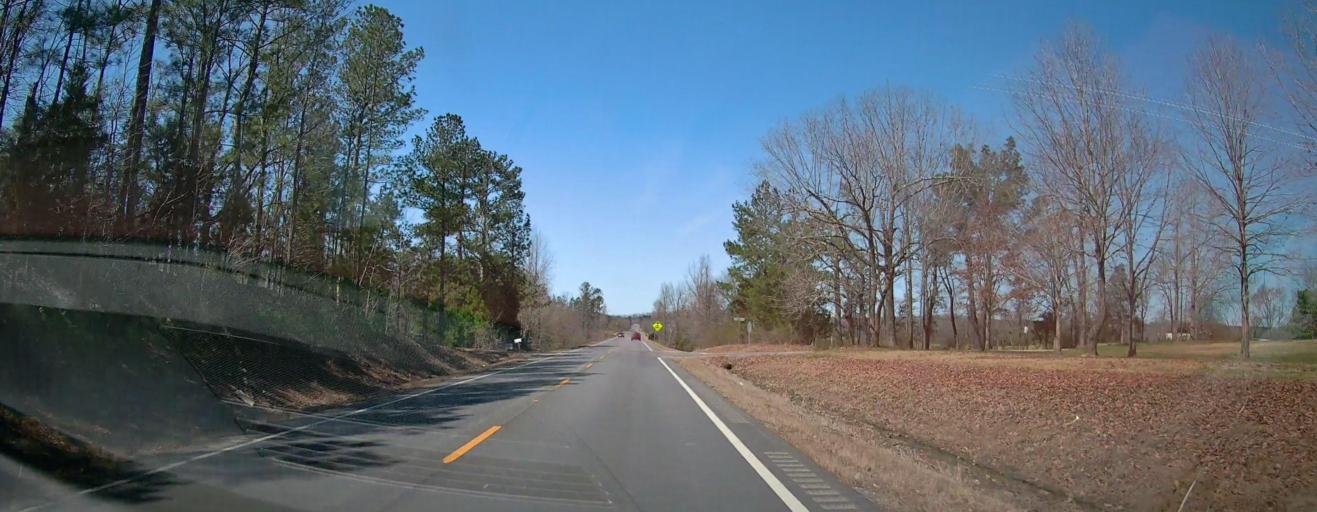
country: US
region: Alabama
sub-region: Calhoun County
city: Ohatchee
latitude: 33.7747
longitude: -85.9906
